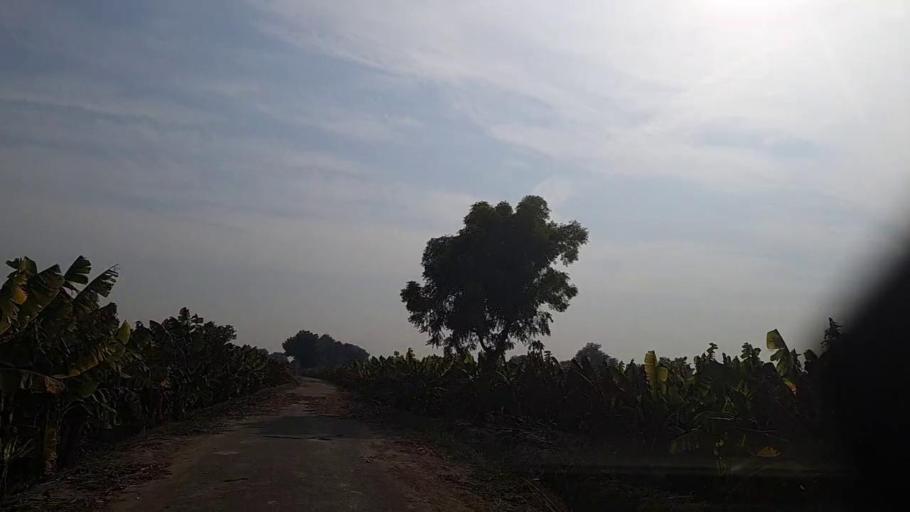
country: PK
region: Sindh
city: Daur
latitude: 26.3977
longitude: 68.2016
